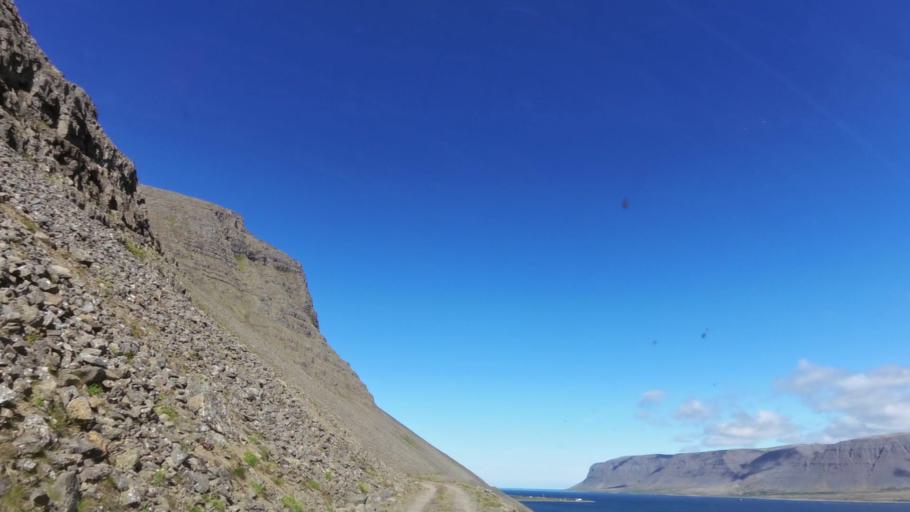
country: IS
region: West
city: Olafsvik
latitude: 65.6281
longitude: -23.9049
